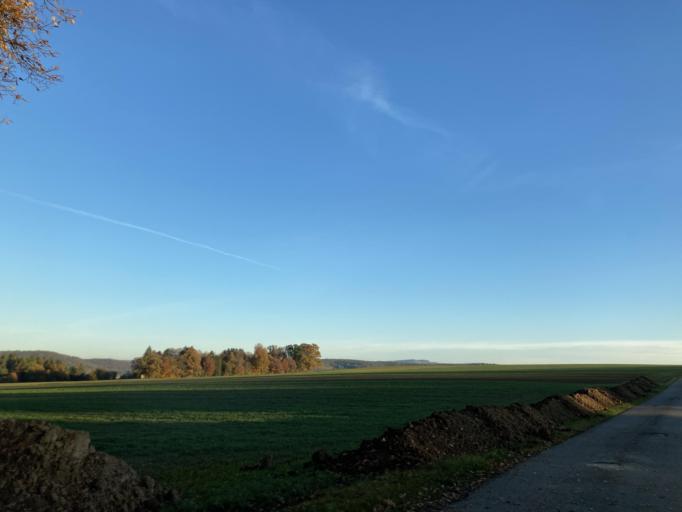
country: DE
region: Baden-Wuerttemberg
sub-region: Tuebingen Region
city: Hirrlingen
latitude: 48.4381
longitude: 8.8970
